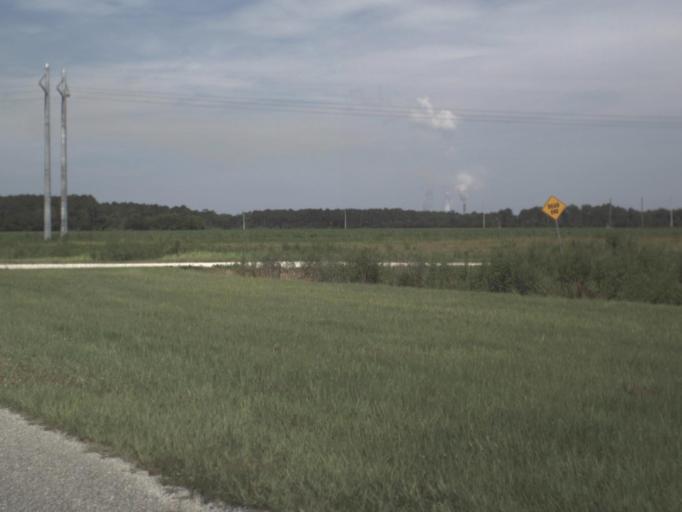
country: US
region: Florida
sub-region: Putnam County
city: East Palatka
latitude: 29.7062
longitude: -81.5394
